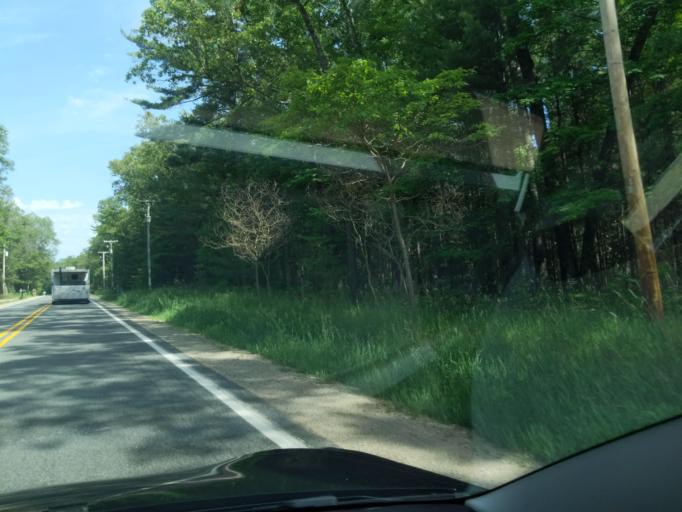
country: US
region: Michigan
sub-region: Muskegon County
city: Lakewood Club
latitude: 43.4082
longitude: -86.2760
